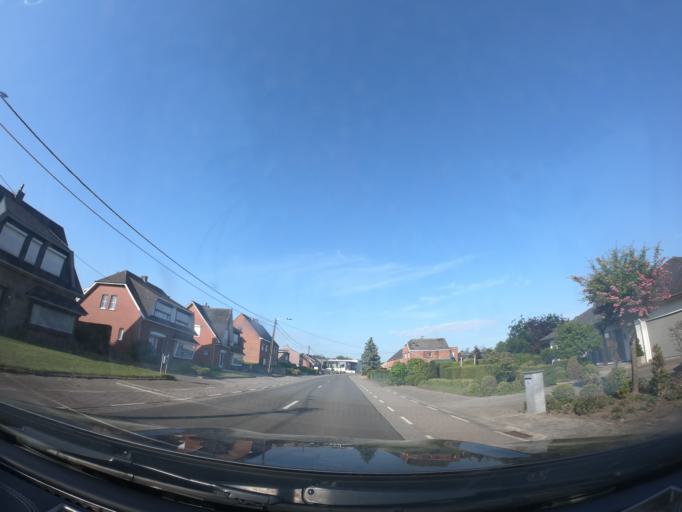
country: BE
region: Flanders
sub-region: Provincie Antwerpen
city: Geel
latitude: 51.1655
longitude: 4.9310
